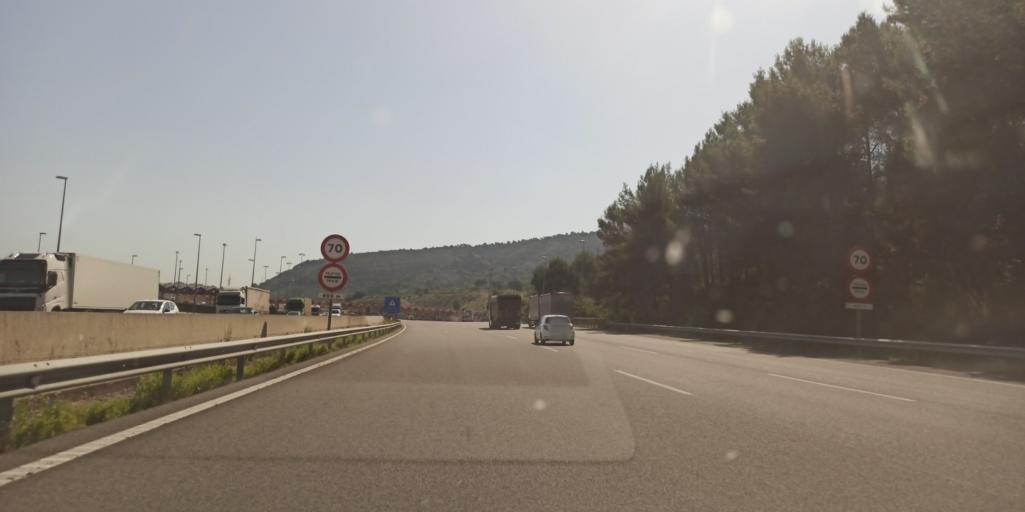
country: ES
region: Catalonia
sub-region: Provincia de Barcelona
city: Castellvi de Rosanes
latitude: 41.4632
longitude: 1.9049
